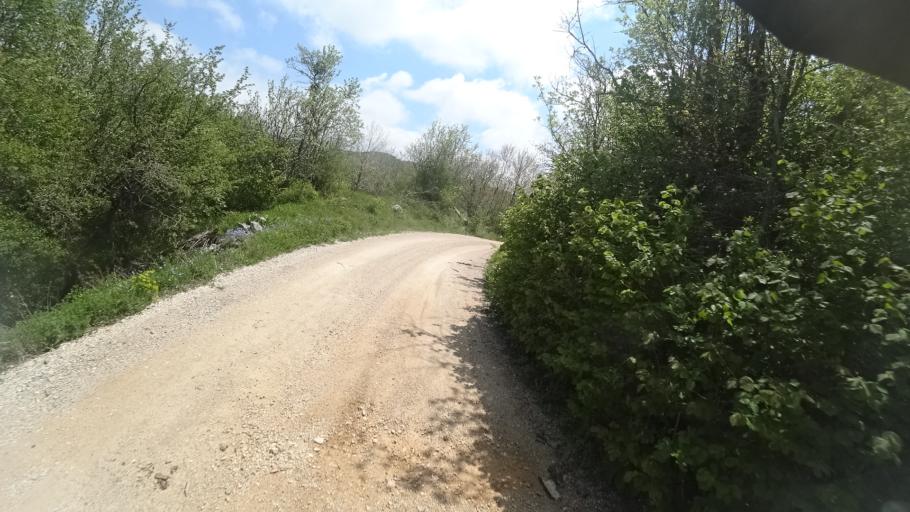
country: HR
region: Zadarska
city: Gracac
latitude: 44.5092
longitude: 15.8861
